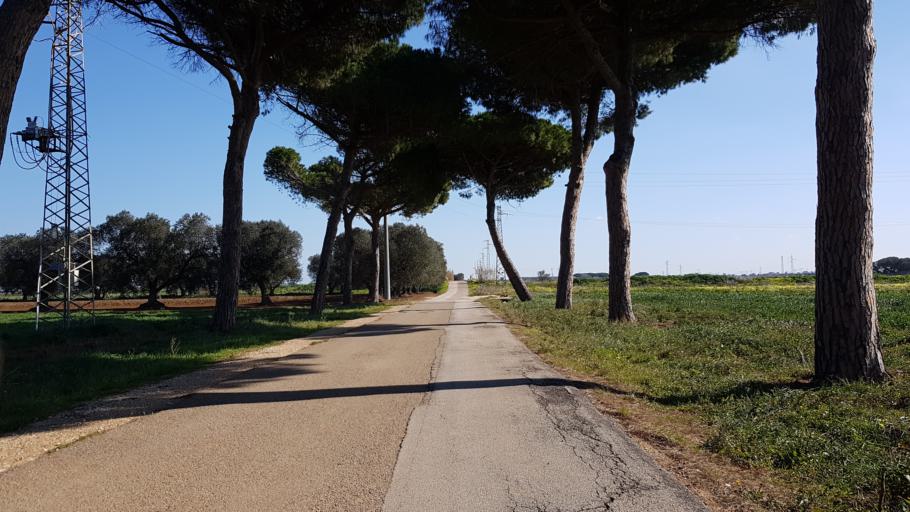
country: IT
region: Apulia
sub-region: Provincia di Brindisi
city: Mesagne
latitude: 40.6194
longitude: 17.8553
